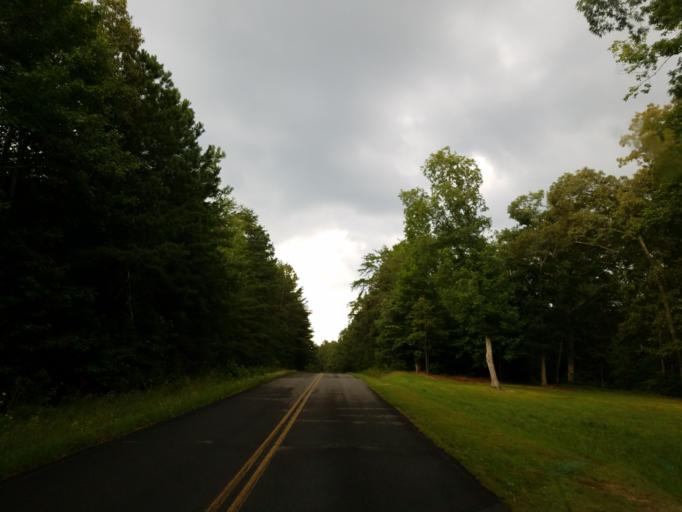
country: US
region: Georgia
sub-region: Whitfield County
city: Dalton
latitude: 34.6478
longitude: -85.0908
